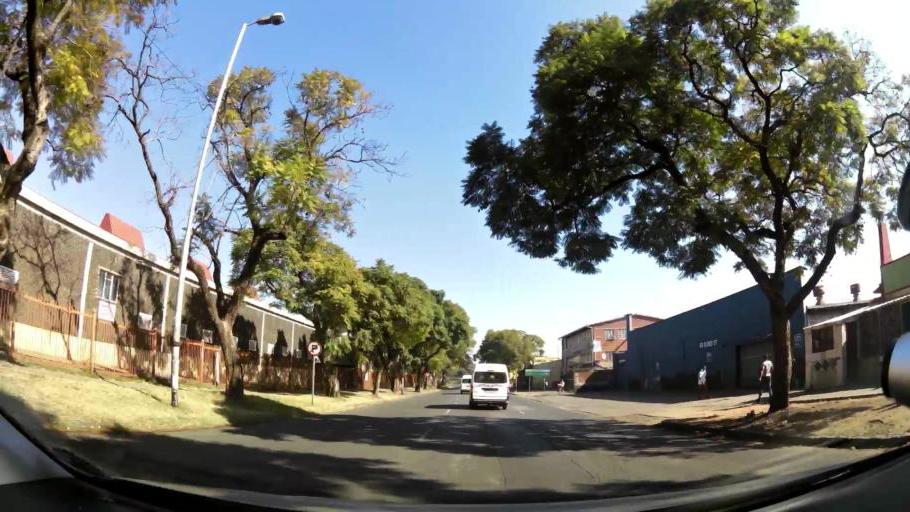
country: ZA
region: Gauteng
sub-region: City of Tshwane Metropolitan Municipality
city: Pretoria
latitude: -25.7410
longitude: 28.1815
